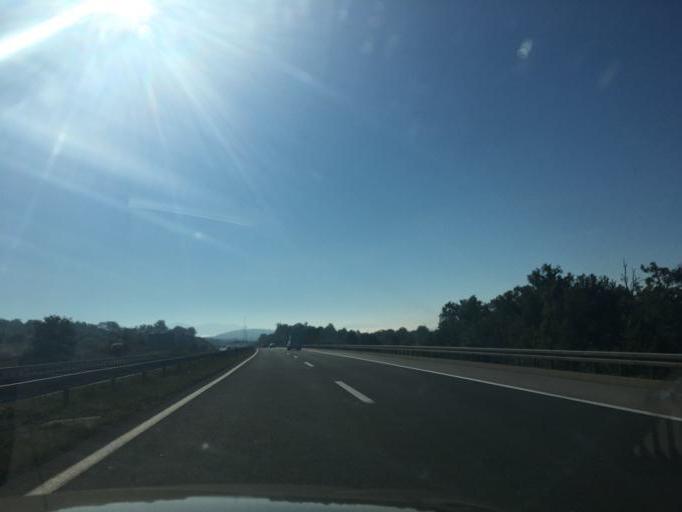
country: HR
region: Licko-Senjska
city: Gospic
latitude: 44.6768
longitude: 15.4123
